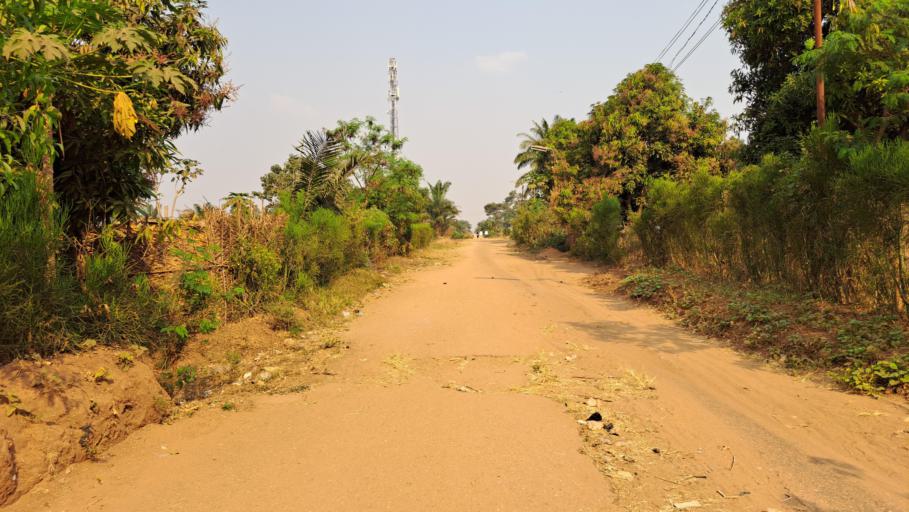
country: CD
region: Kasai-Oriental
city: Mbuji-Mayi
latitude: -6.1387
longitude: 23.5908
